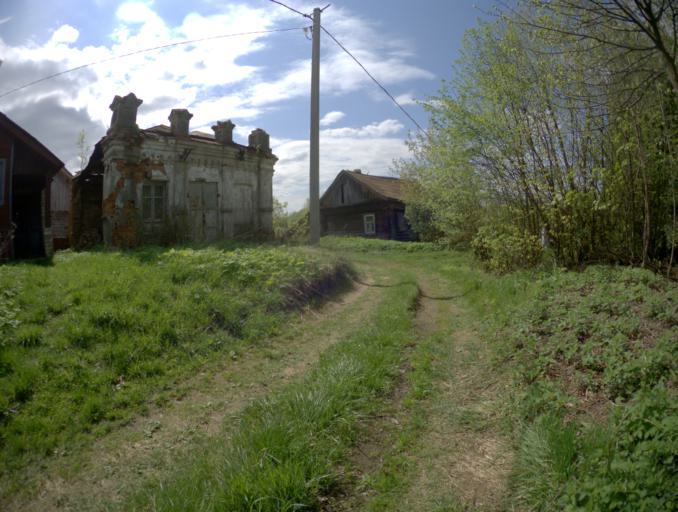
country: RU
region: Vladimir
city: Golovino
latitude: 56.0042
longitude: 40.4333
